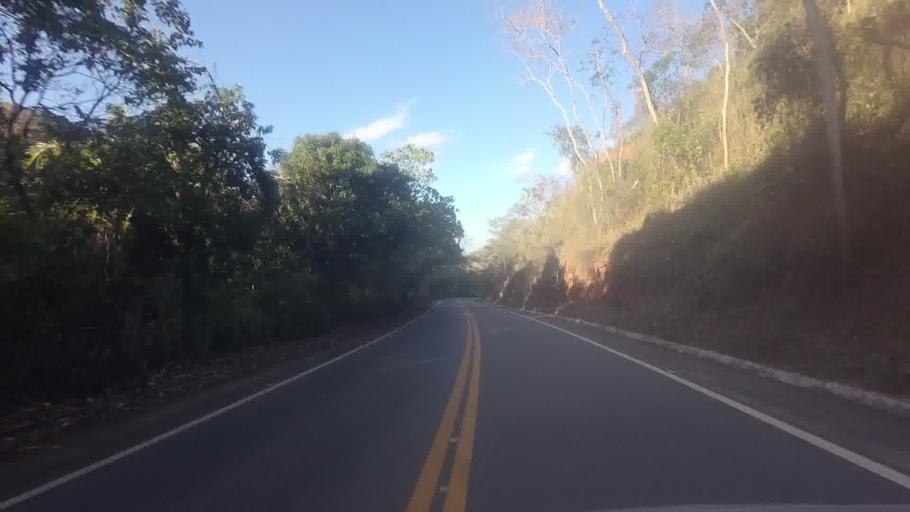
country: BR
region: Espirito Santo
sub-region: Cachoeiro De Itapemirim
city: Cachoeiro de Itapemirim
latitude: -20.8406
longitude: -41.2345
